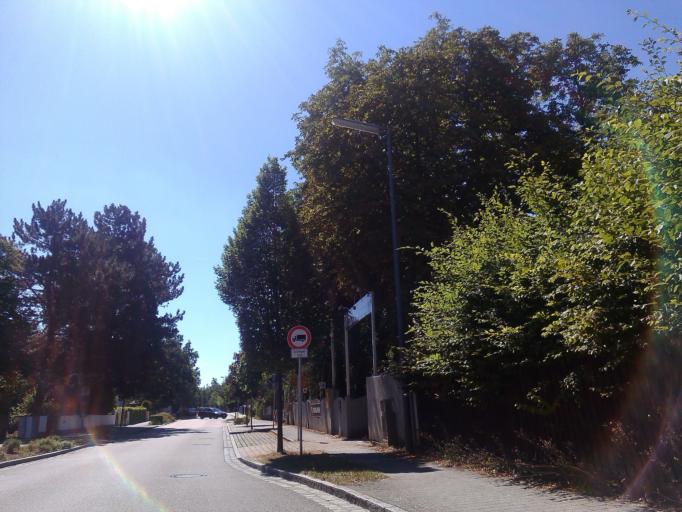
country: DE
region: Bavaria
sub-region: Upper Bavaria
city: Grafelfing
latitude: 48.1370
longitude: 11.4272
